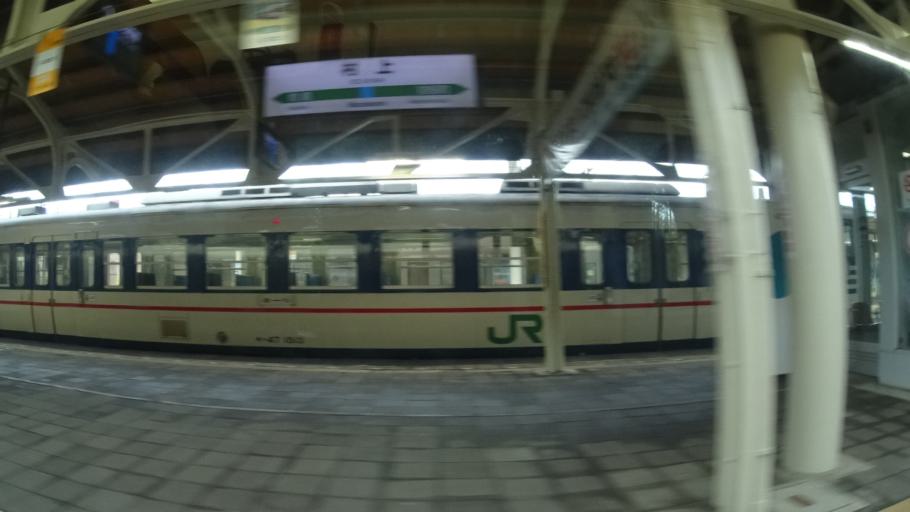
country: JP
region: Niigata
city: Murakami
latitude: 38.2204
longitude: 139.4634
